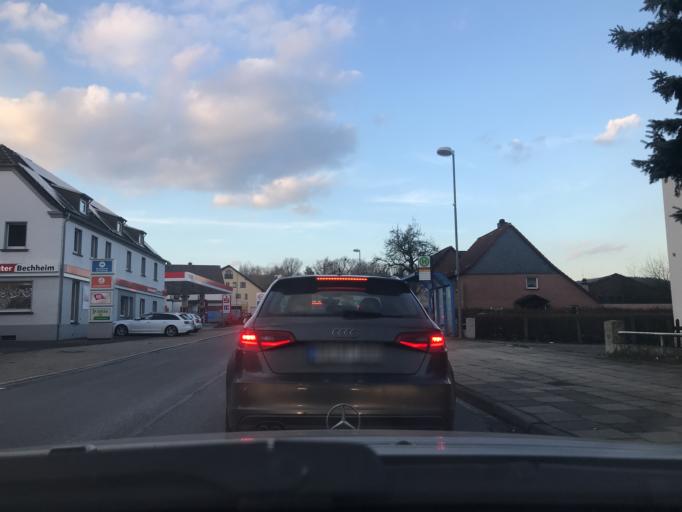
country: DE
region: North Rhine-Westphalia
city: Wickede
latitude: 51.5001
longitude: 7.8705
